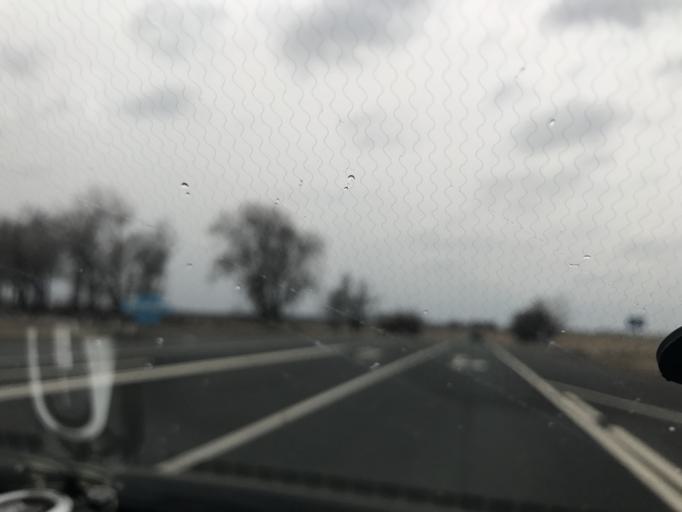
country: RU
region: Krasnodarskiy
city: Novoleushkovskaya
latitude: 46.0118
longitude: 40.0106
